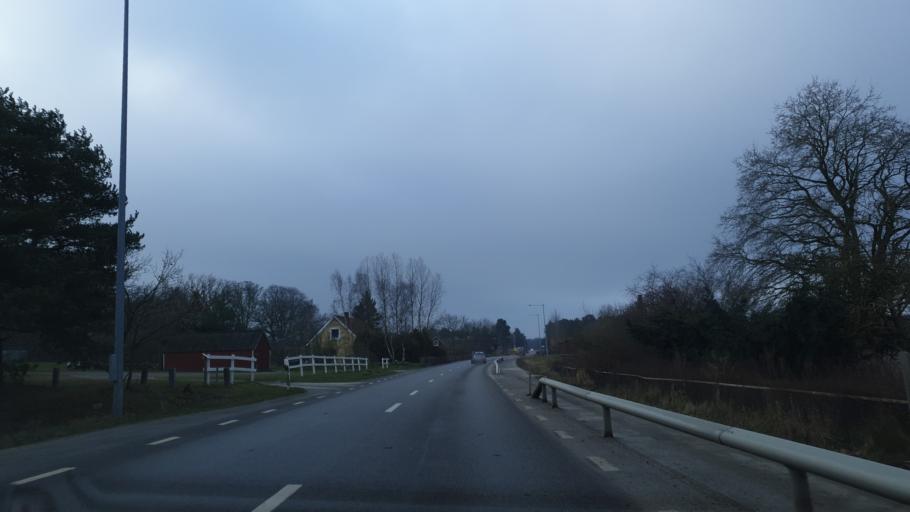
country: SE
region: Blekinge
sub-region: Solvesborgs Kommun
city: Soelvesborg
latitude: 56.1037
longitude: 14.6692
